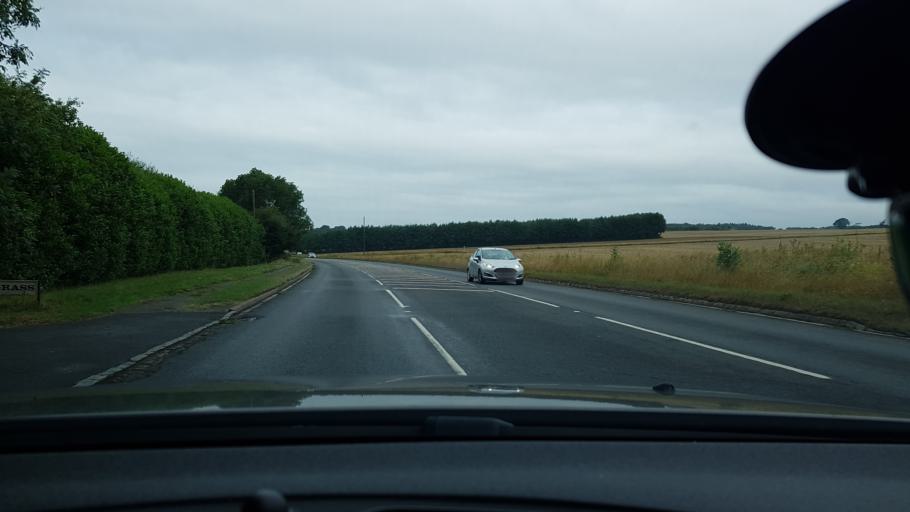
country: GB
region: England
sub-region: Wiltshire
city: Chilton Foliat
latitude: 51.4180
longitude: -1.5317
